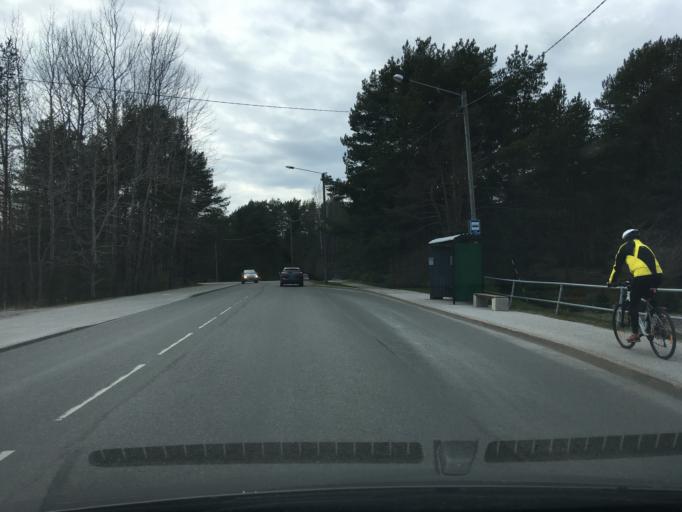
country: EE
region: Harju
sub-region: Tallinna linn
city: Kose
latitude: 59.4730
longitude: 24.9124
